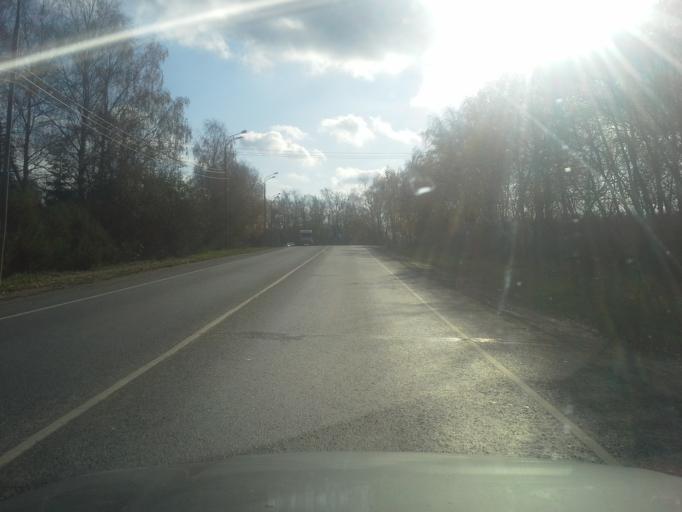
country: RU
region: Moskovskaya
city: Zvenigorod
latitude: 55.6846
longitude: 36.9017
